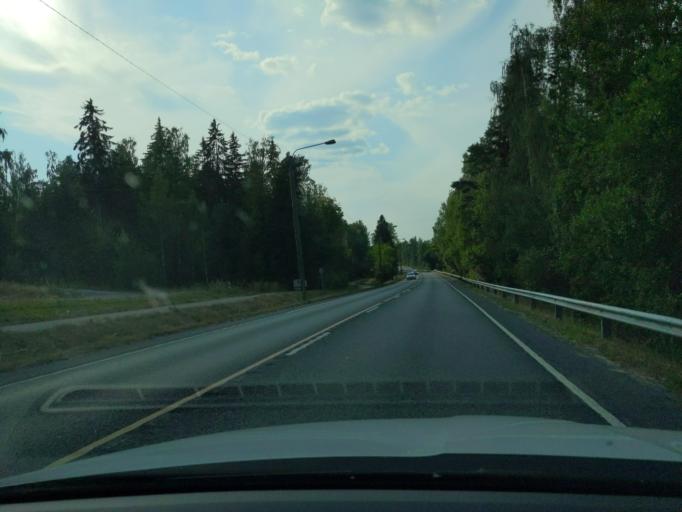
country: FI
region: Paijanne Tavastia
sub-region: Lahti
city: Asikkala
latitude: 61.1677
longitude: 25.5598
